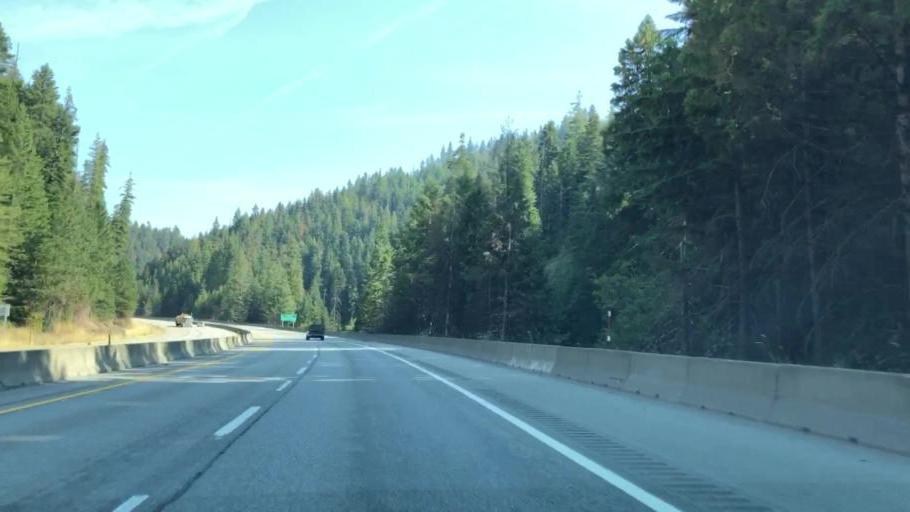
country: US
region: Idaho
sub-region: Kootenai County
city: Coeur d'Alene
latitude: 47.6288
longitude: -116.5967
